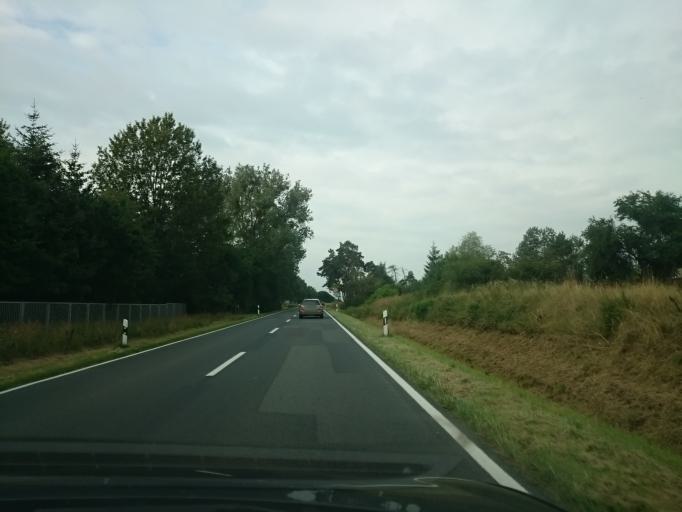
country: DE
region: Mecklenburg-Vorpommern
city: Mollenhagen
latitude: 53.5507
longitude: 12.8518
